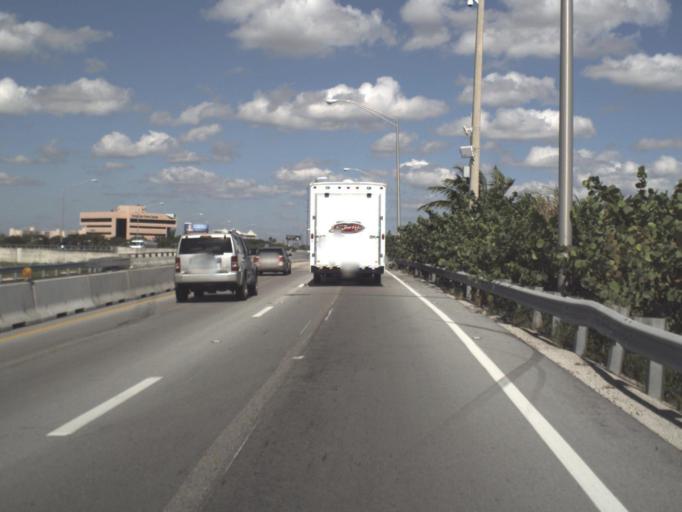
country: US
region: Florida
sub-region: Miami-Dade County
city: Cutler Ridge
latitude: 25.5722
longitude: -80.3631
